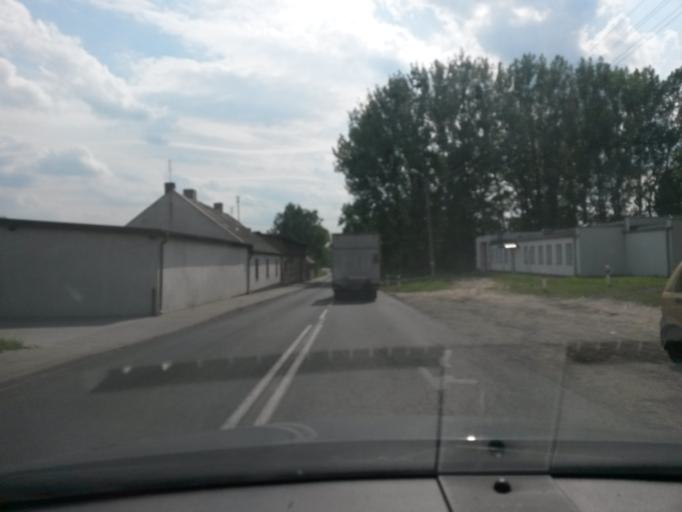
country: PL
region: Greater Poland Voivodeship
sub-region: Powiat poznanski
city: Kleszczewo
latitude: 52.3018
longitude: 17.1256
